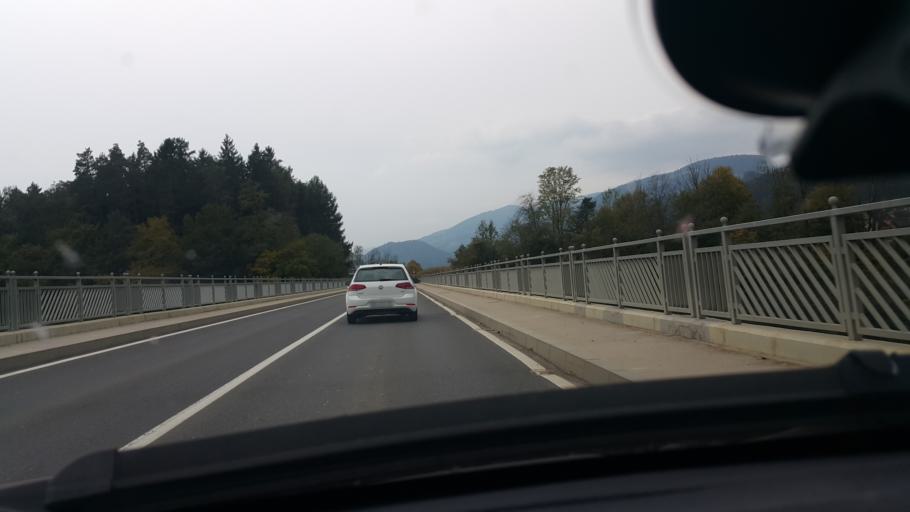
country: SI
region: Radlje ob Dravi
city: Radlje ob Dravi
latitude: 46.6142
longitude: 15.2056
